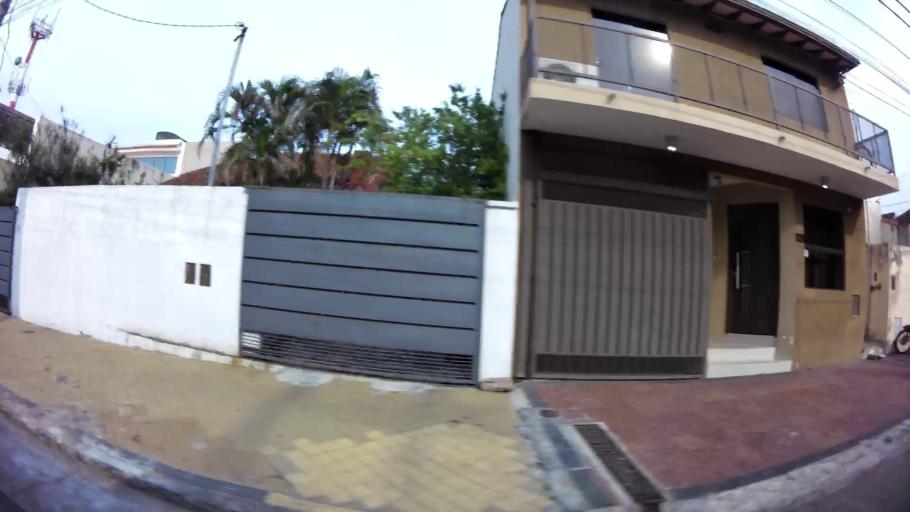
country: PY
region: Asuncion
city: Asuncion
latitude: -25.2966
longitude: -57.6167
